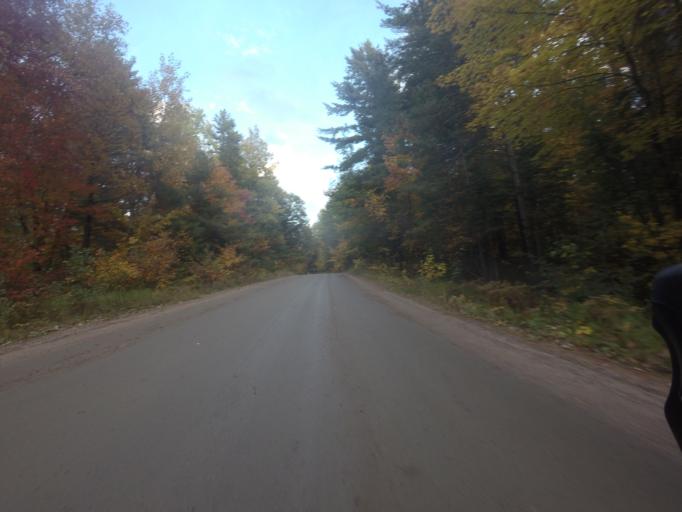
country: CA
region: Ontario
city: Deep River
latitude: 45.8937
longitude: -77.6195
